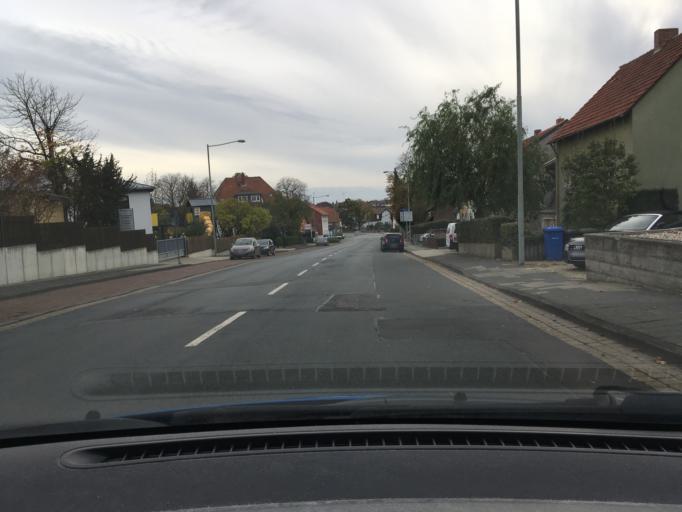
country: DE
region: Lower Saxony
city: Helmstedt
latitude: 52.2360
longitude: 11.0089
